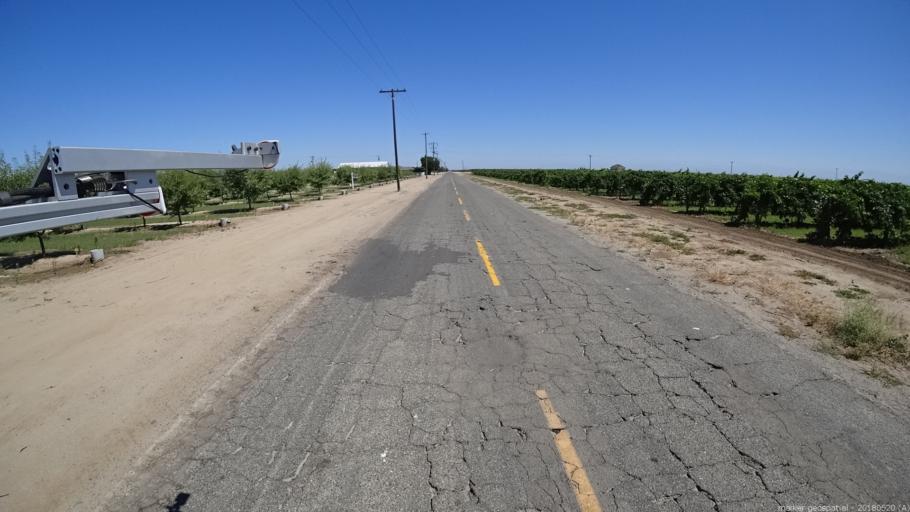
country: US
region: California
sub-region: Fresno County
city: Biola
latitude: 36.8642
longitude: -120.0013
